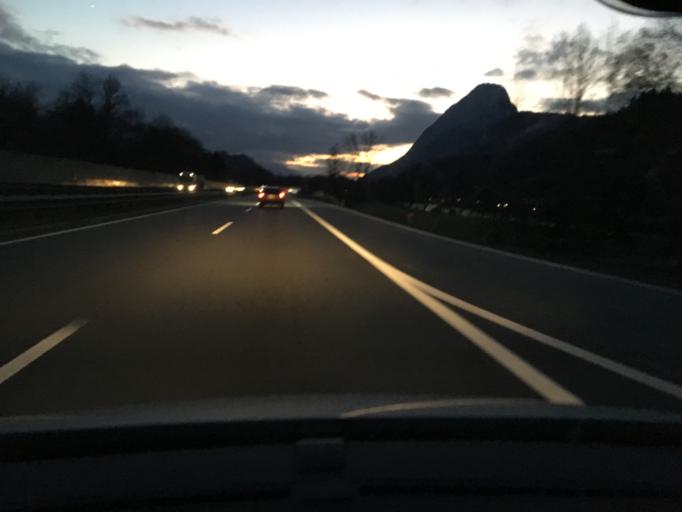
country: AT
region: Tyrol
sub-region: Politischer Bezirk Kufstein
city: Kufstein
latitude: 47.5977
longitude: 12.1772
